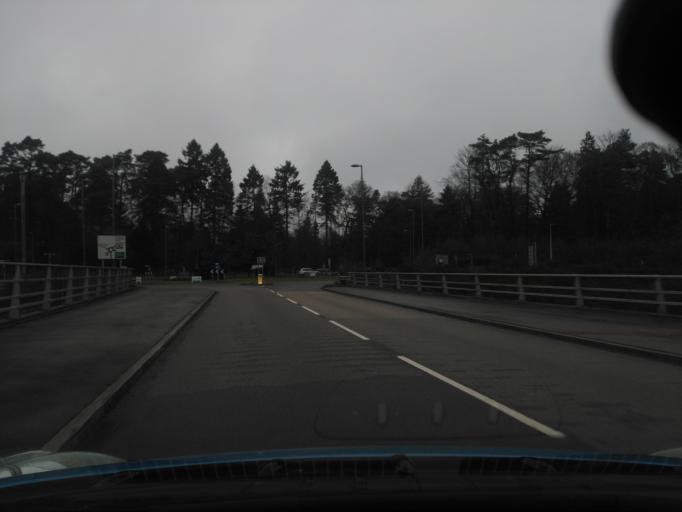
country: GB
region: England
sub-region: Surrey
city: Hindhead
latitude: 51.1061
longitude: -0.7425
